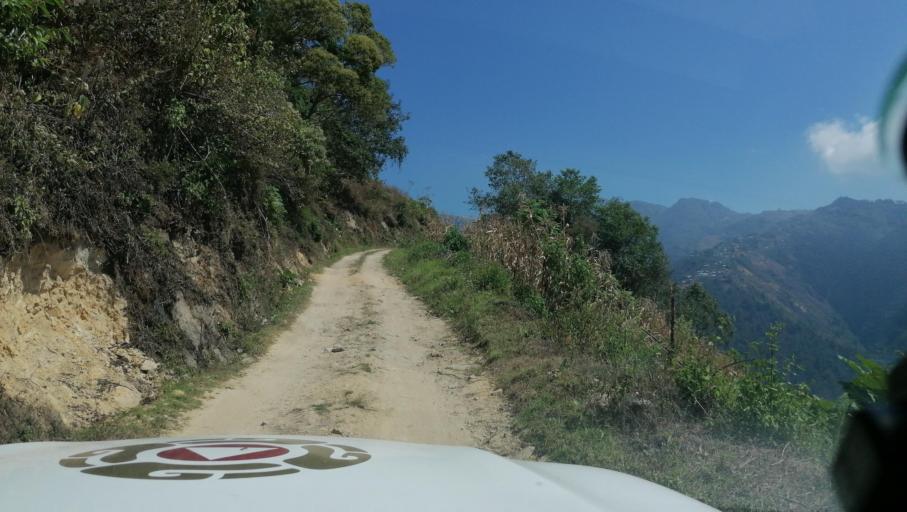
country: GT
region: San Marcos
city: Tacana
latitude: 15.2080
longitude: -92.2151
